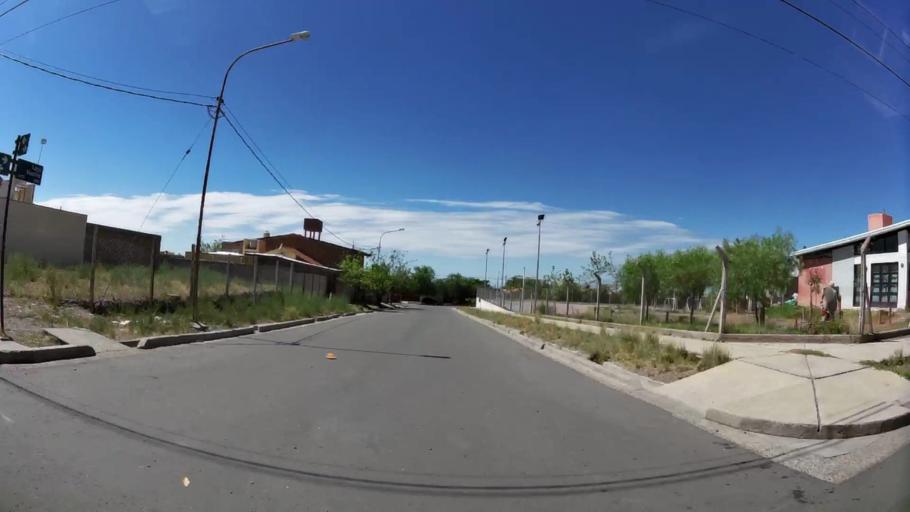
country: AR
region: Mendoza
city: Las Heras
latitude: -32.8464
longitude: -68.8747
